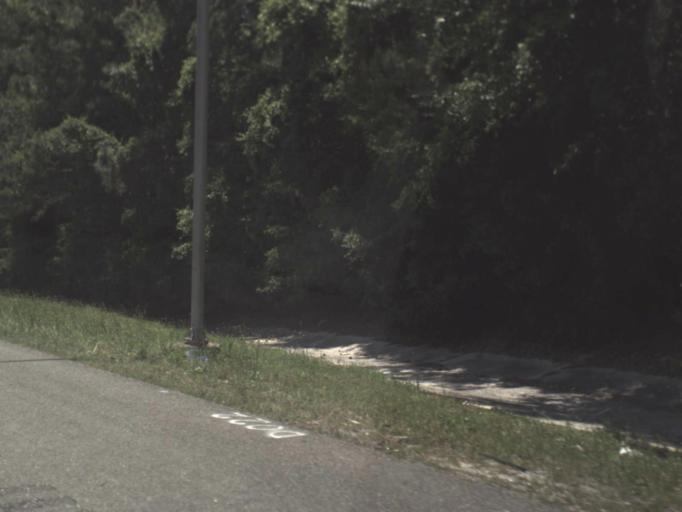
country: US
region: Florida
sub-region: Clay County
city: Bellair-Meadowbrook Terrace
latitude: 30.2867
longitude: -81.7718
